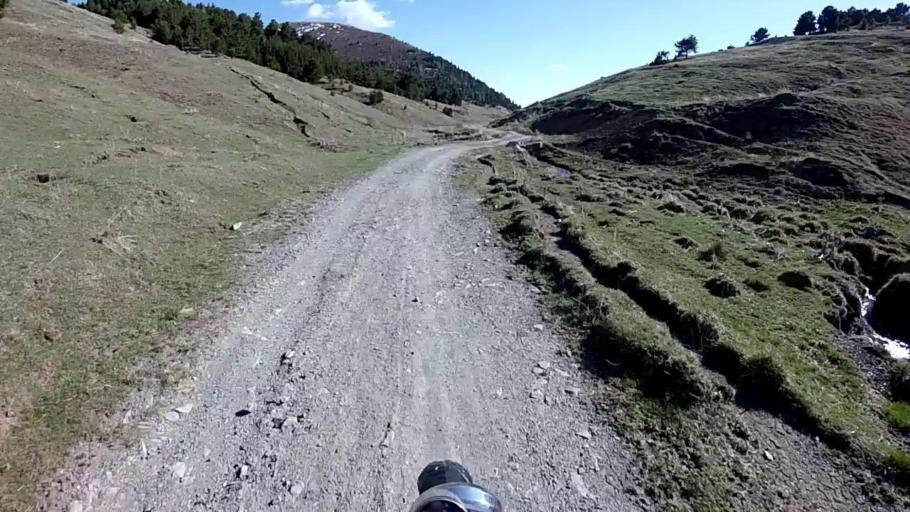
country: FR
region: Provence-Alpes-Cote d'Azur
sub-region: Departement des Alpes-de-Haute-Provence
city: Seyne-les-Alpes
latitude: 44.3203
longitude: 6.3007
